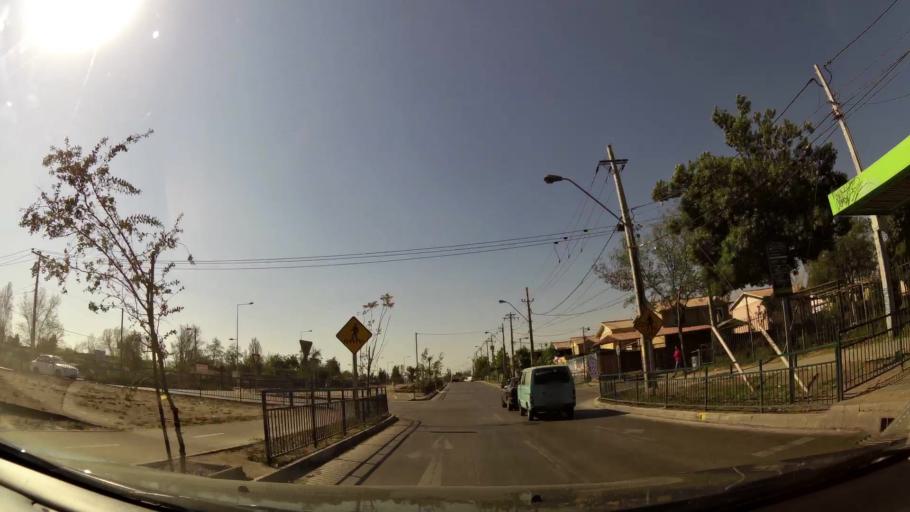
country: CL
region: Santiago Metropolitan
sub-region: Provincia de Santiago
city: La Pintana
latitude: -33.6213
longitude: -70.6272
